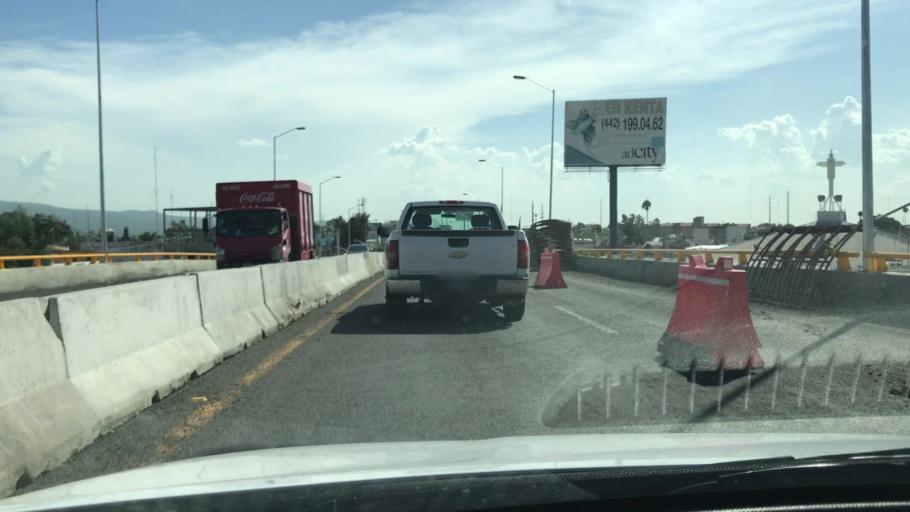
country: MX
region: Guanajuato
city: Celaya
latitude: 20.5159
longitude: -100.7947
